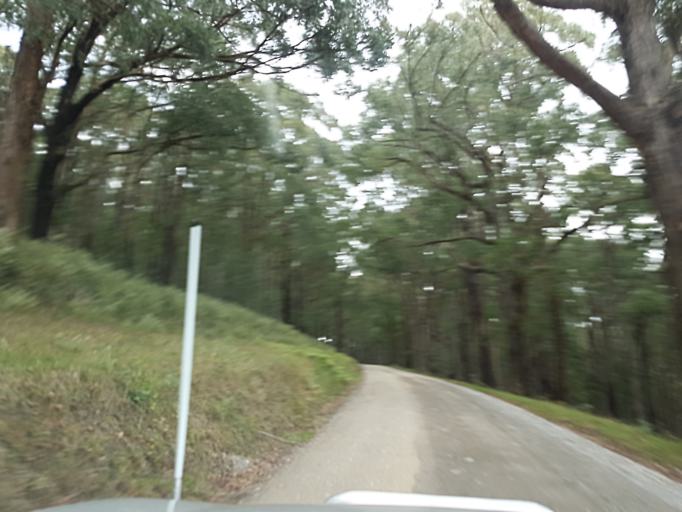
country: AU
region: Victoria
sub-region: Yarra Ranges
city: Olinda
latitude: -37.8512
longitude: 145.3887
